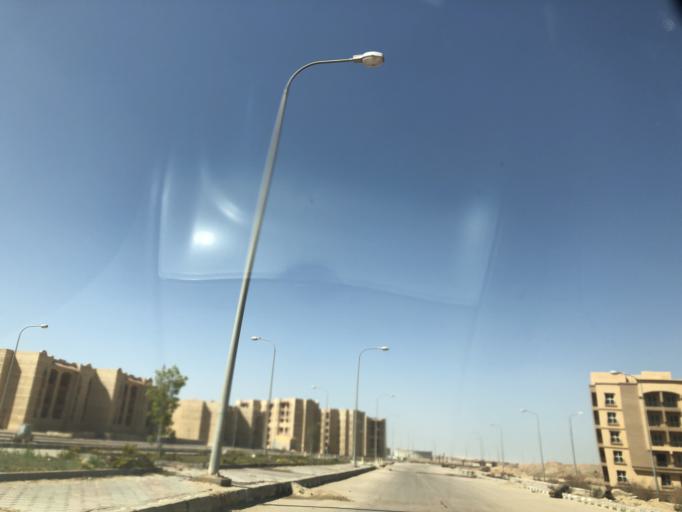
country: EG
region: Al Jizah
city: Madinat Sittah Uktubar
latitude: 29.9227
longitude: 31.0377
